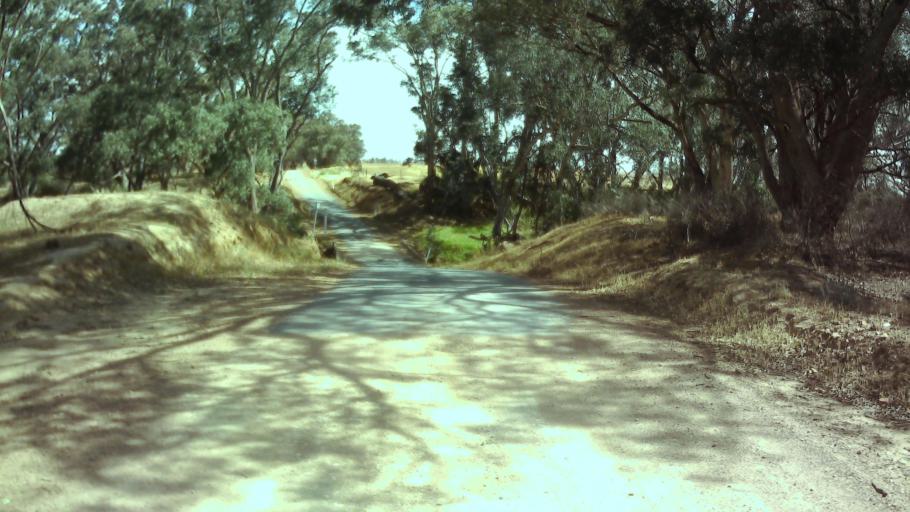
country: AU
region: New South Wales
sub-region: Weddin
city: Grenfell
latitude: -34.0410
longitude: 148.0796
